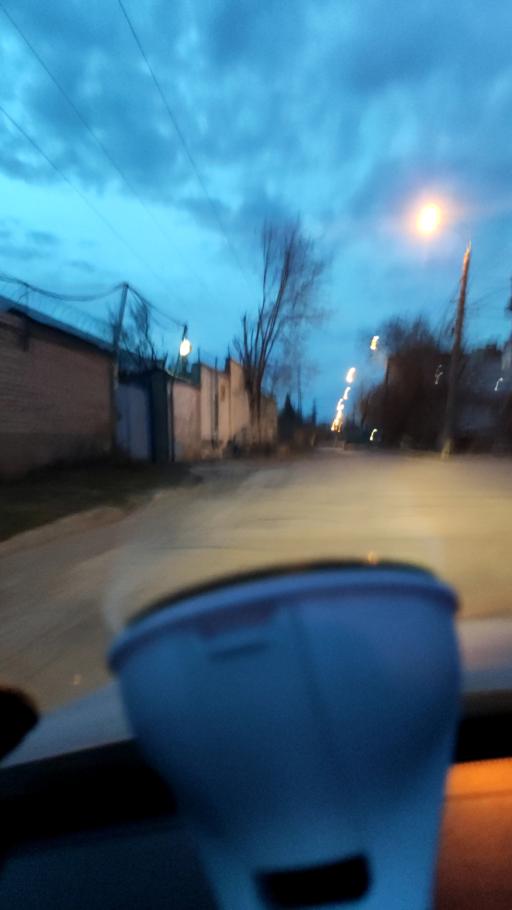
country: RU
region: Samara
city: Volzhskiy
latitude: 53.3495
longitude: 50.2087
